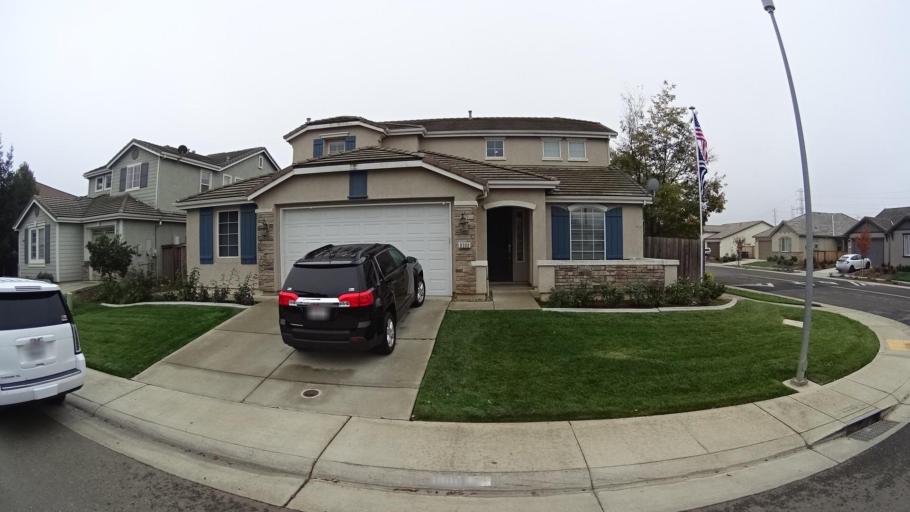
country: US
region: California
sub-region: Sacramento County
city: Elk Grove
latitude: 38.4001
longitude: -121.3480
